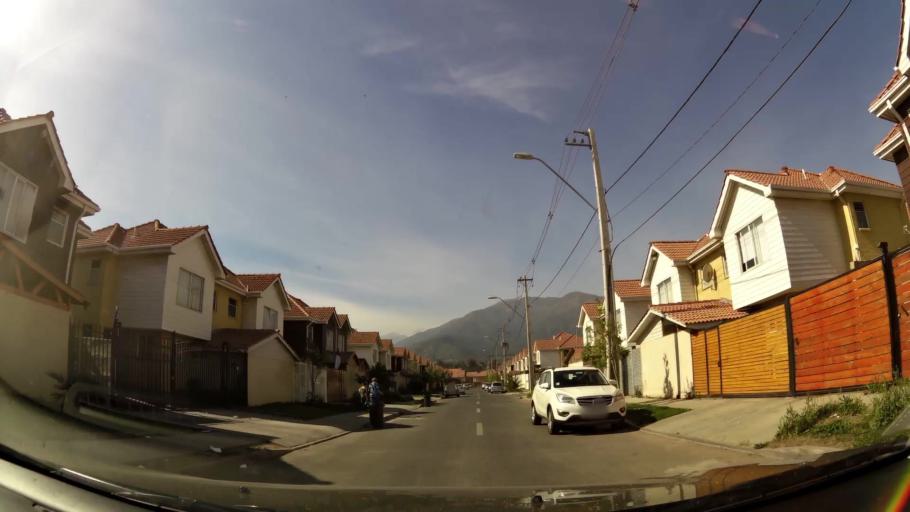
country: CL
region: Santiago Metropolitan
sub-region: Provincia de Cordillera
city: Puente Alto
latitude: -33.5940
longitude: -70.5474
